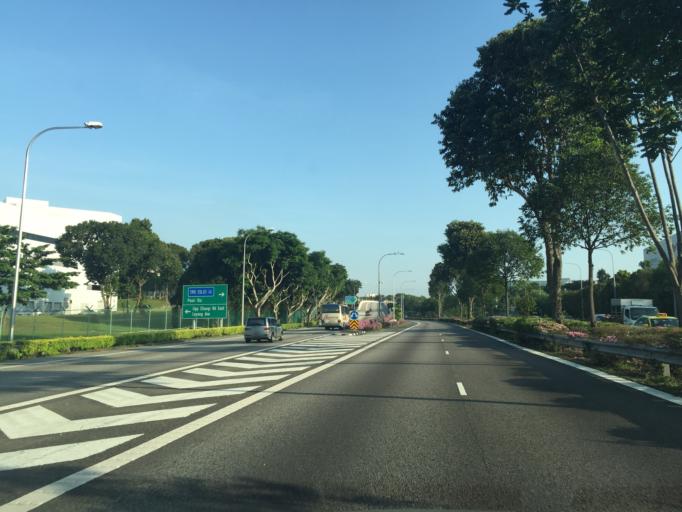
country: SG
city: Singapore
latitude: 1.3459
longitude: 103.9676
